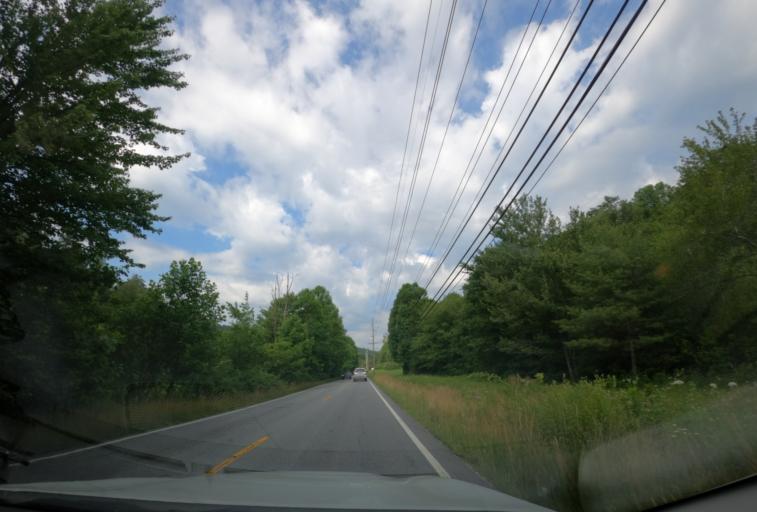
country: US
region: North Carolina
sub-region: Jackson County
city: Cullowhee
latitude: 35.1290
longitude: -83.0696
